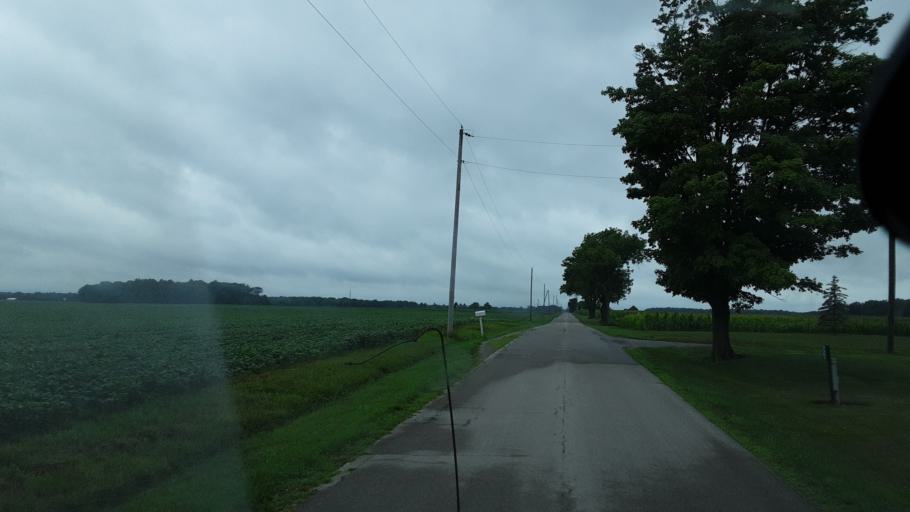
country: US
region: Ohio
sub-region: Van Wert County
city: Convoy
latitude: 40.8296
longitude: -84.7572
